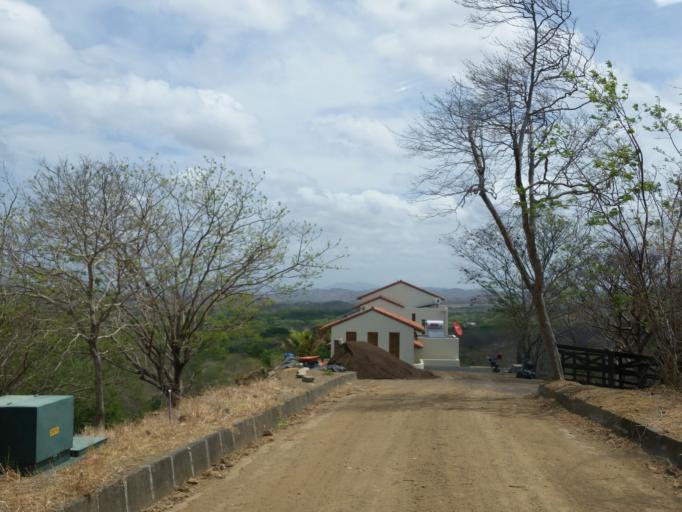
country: NI
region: Rivas
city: Tola
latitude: 11.4364
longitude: -86.0796
